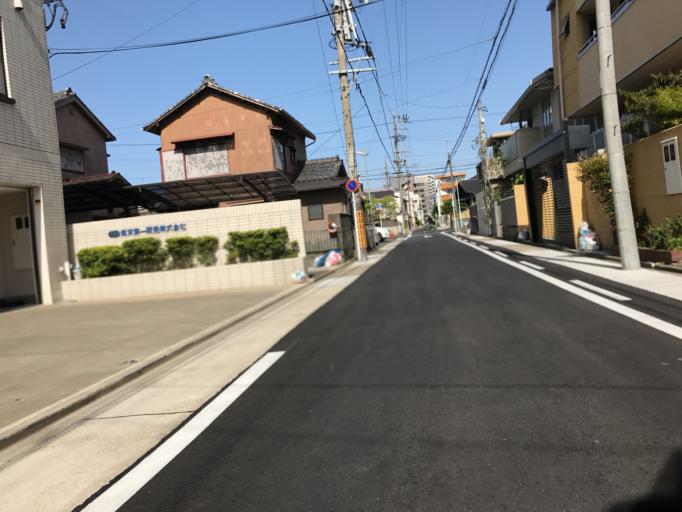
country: JP
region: Aichi
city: Nagoya-shi
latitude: 35.1722
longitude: 136.9417
